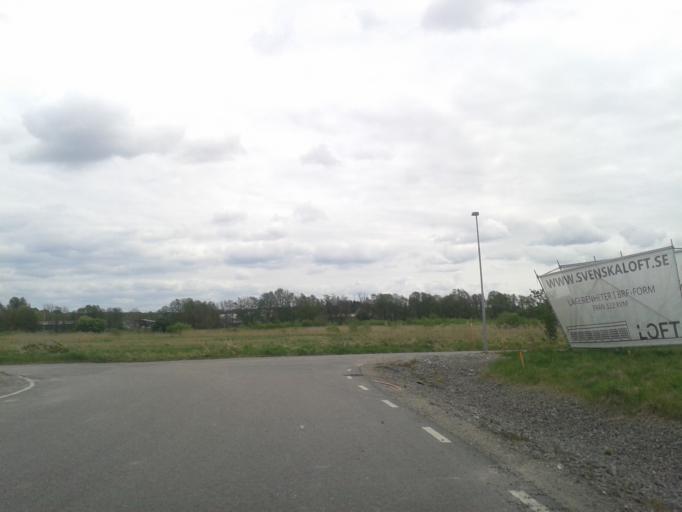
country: SE
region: Vaestra Goetaland
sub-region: Kungalvs Kommun
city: Kungalv
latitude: 57.8966
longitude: 11.9314
